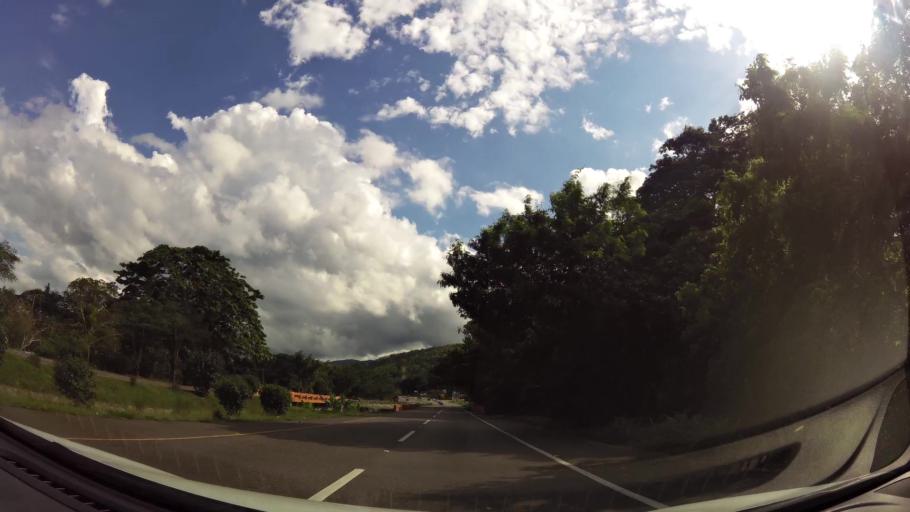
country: DO
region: La Vega
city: Concepcion de La Vega
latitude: 19.1868
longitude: -70.4985
